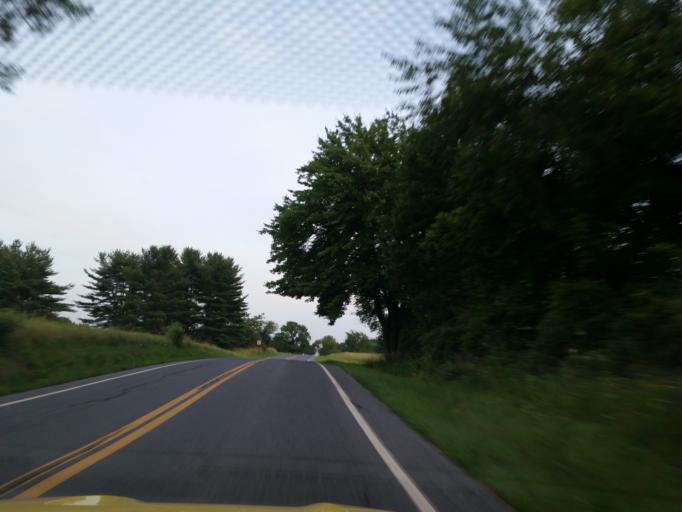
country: US
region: Pennsylvania
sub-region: Lebanon County
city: Palmyra
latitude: 40.4178
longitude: -76.6074
